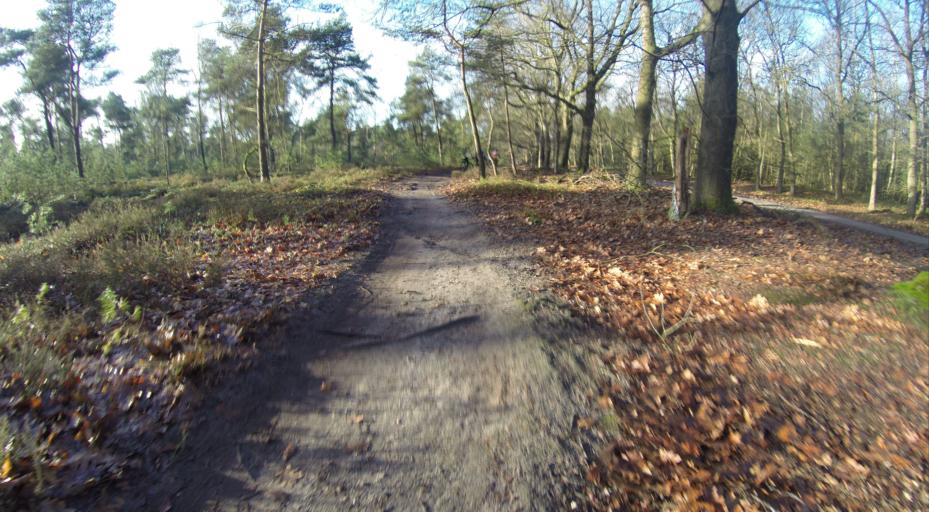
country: NL
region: Gelderland
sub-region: Gemeente Lochem
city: Laren
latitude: 52.3229
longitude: 6.3987
